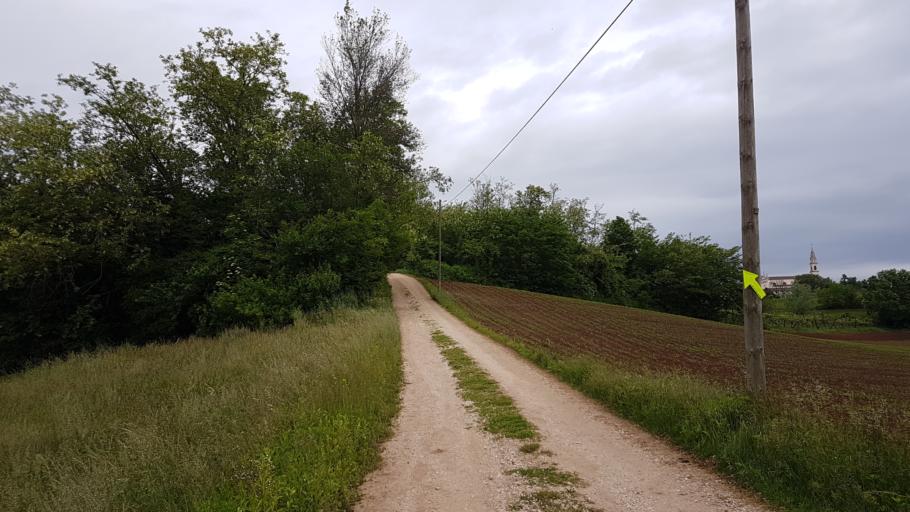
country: IT
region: Veneto
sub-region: Provincia di Vicenza
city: Trissino
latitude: 45.5595
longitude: 11.3364
